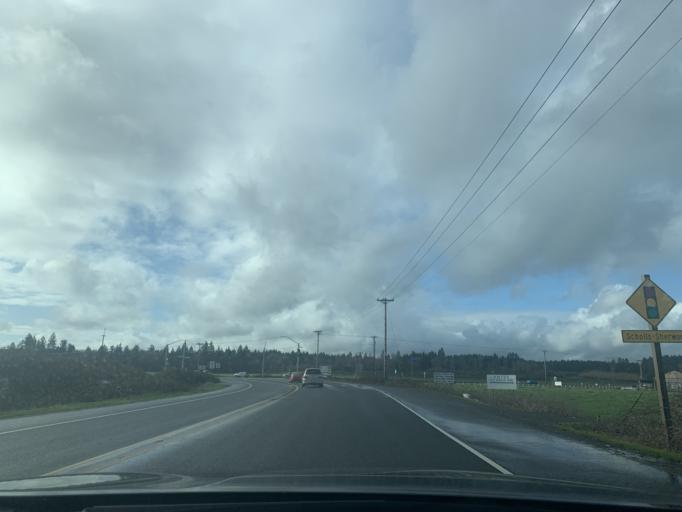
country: US
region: Oregon
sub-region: Washington County
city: Sherwood
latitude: 45.3821
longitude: -122.8548
